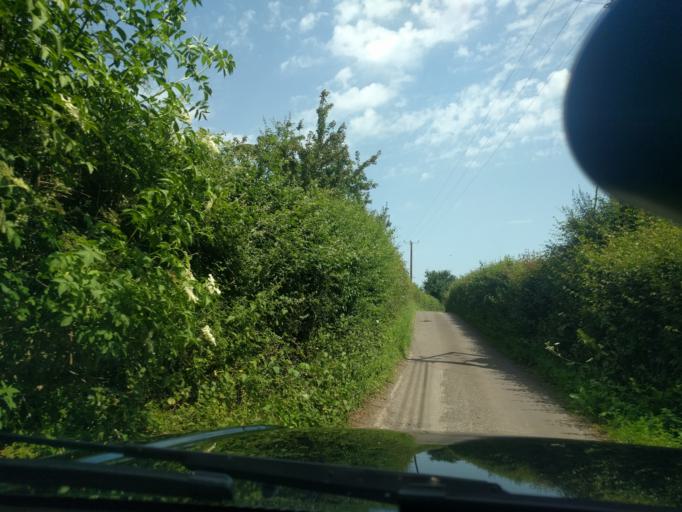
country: GB
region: England
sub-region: Wiltshire
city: Bradford-on-Avon
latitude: 51.3789
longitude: -2.2470
